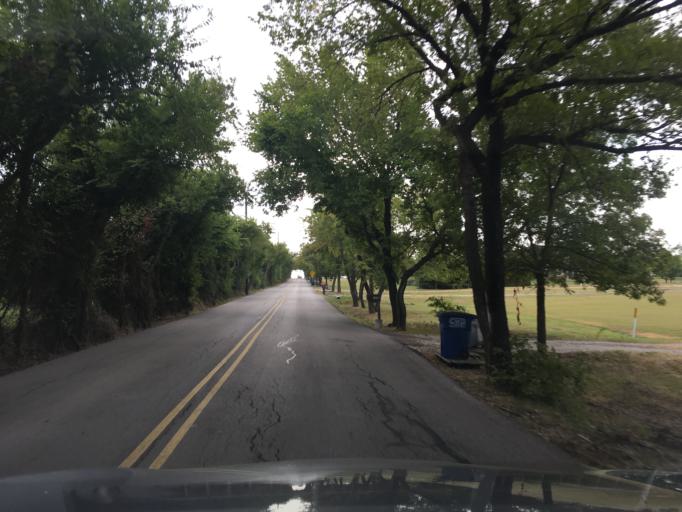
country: US
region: Texas
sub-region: Collin County
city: Saint Paul
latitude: 33.0312
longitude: -96.5741
